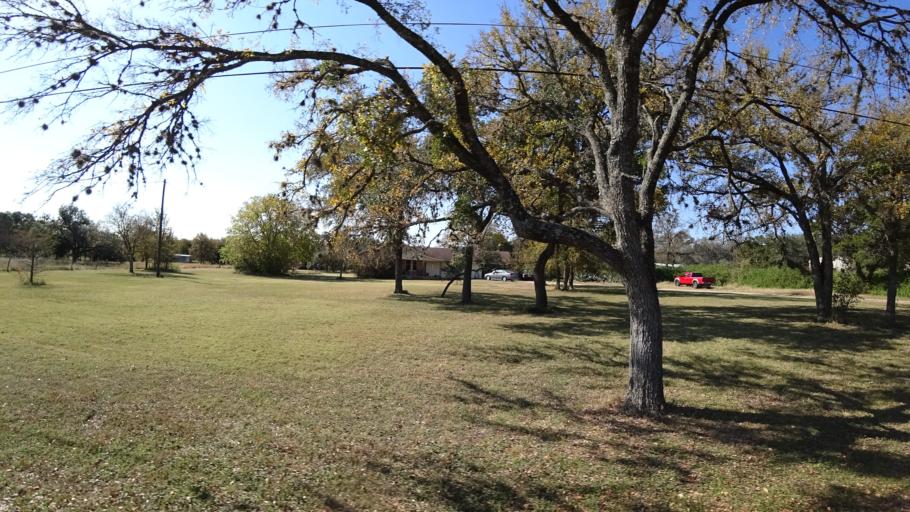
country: US
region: Texas
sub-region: Travis County
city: Barton Creek
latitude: 30.2279
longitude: -97.8578
